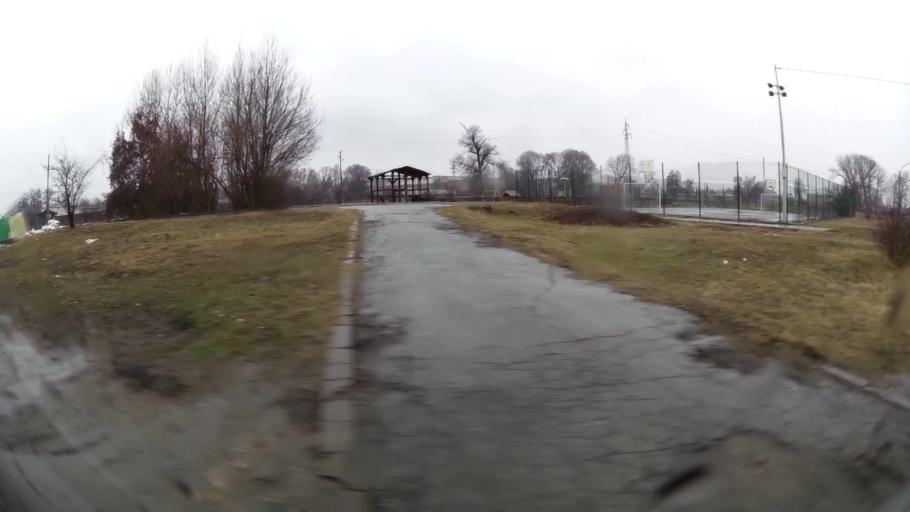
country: BG
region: Sofia-Capital
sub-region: Stolichna Obshtina
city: Sofia
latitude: 42.6585
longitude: 23.4252
